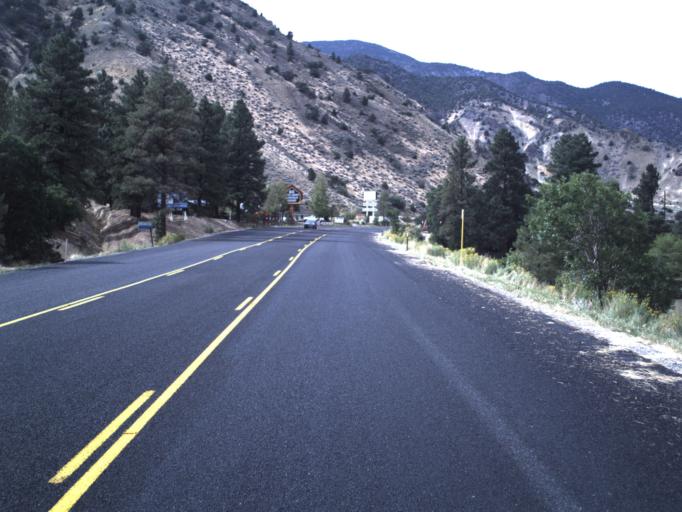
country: US
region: Utah
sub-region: Sevier County
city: Monroe
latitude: 38.5141
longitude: -112.2643
